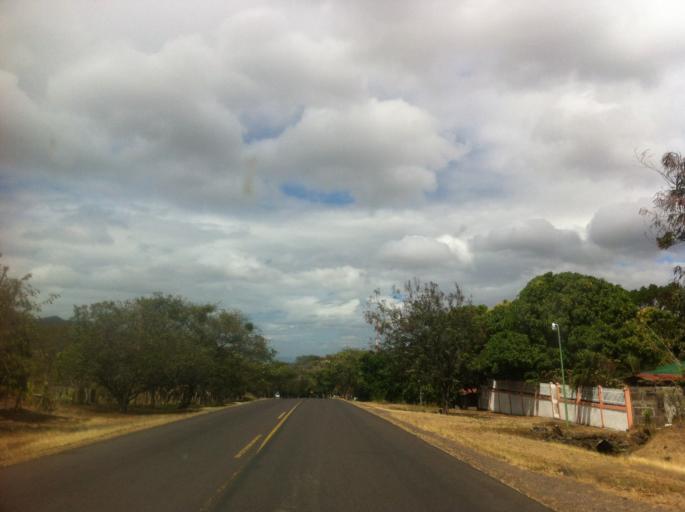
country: NI
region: Chontales
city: Juigalpa
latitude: 12.0464
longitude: -85.2847
